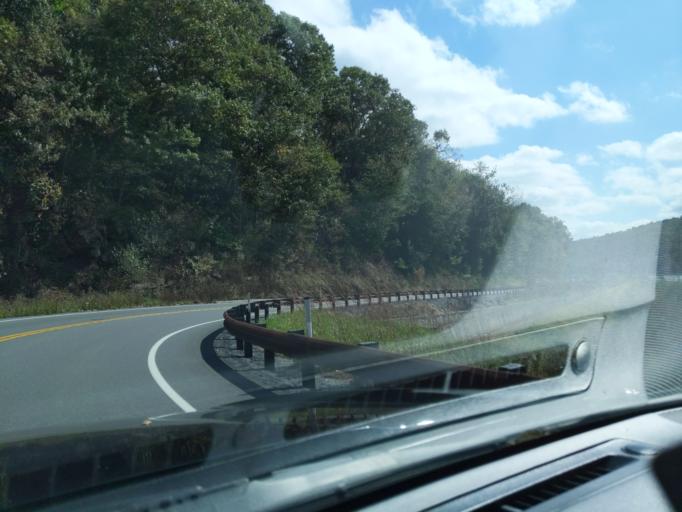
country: US
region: Pennsylvania
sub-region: Blair County
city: Altoona
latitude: 40.4962
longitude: -78.4616
